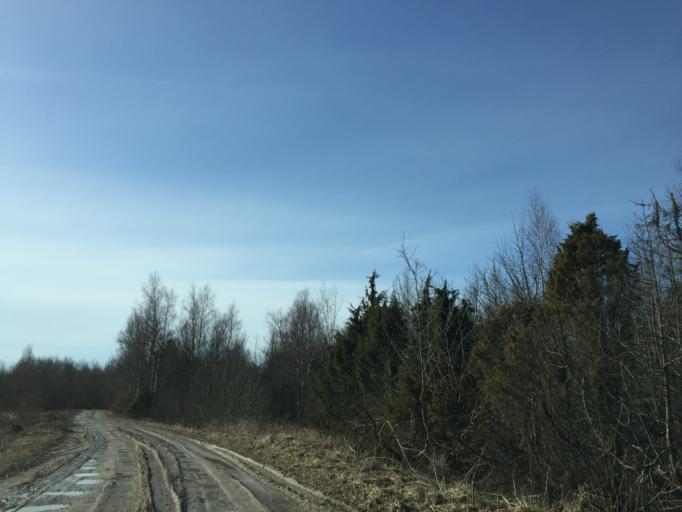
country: EE
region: Laeaene
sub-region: Haapsalu linn
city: Haapsalu
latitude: 58.6583
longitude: 23.5137
